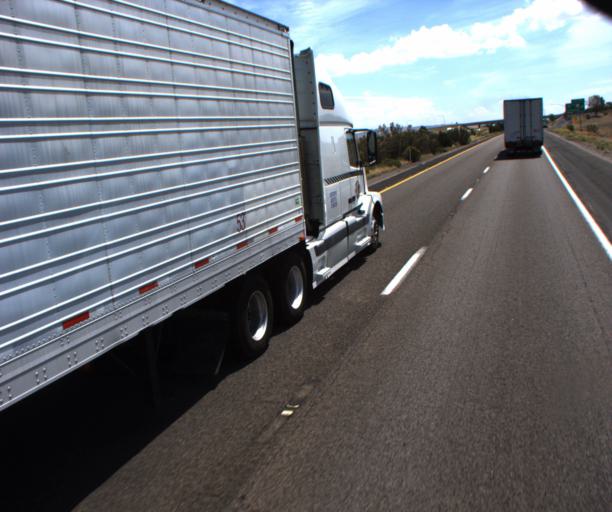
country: US
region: Arizona
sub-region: Mohave County
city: Peach Springs
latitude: 35.3209
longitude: -112.8989
